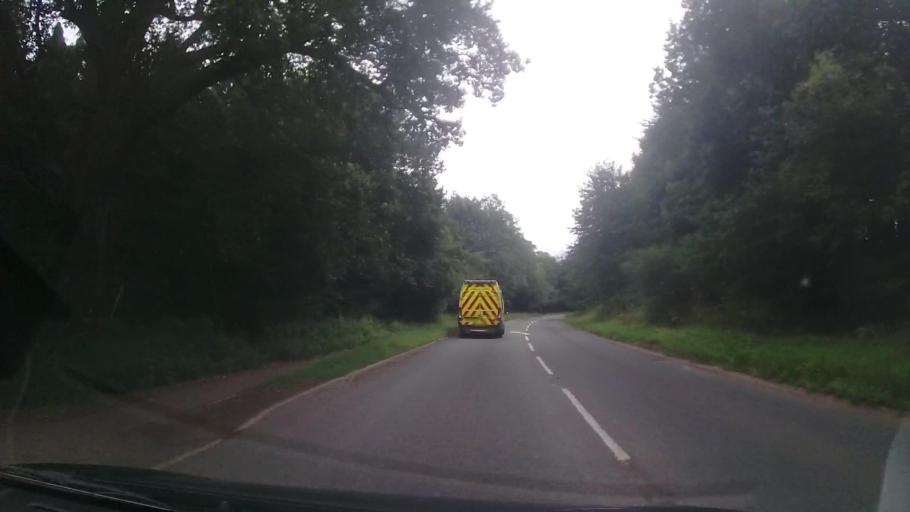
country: GB
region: England
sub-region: Shropshire
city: Bicton
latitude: 52.7181
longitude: -2.7938
